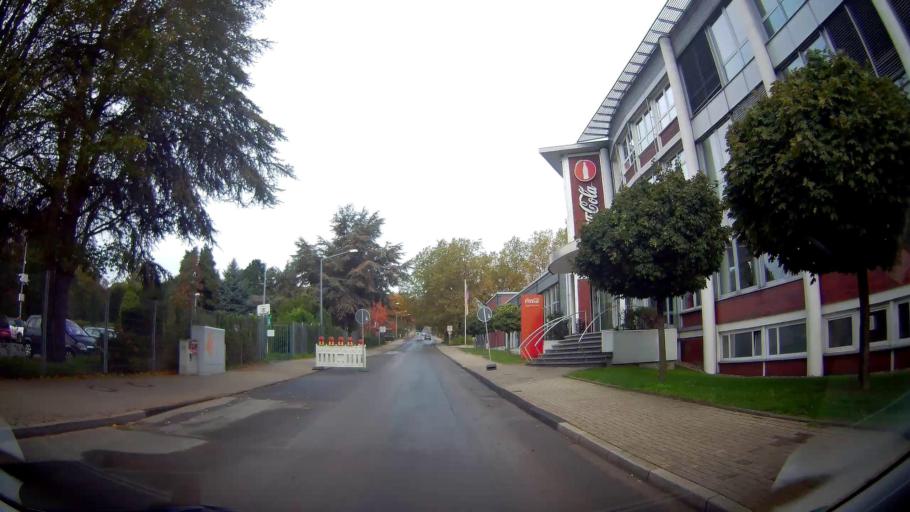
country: DE
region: North Rhine-Westphalia
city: Herten
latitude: 51.5962
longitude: 7.1311
